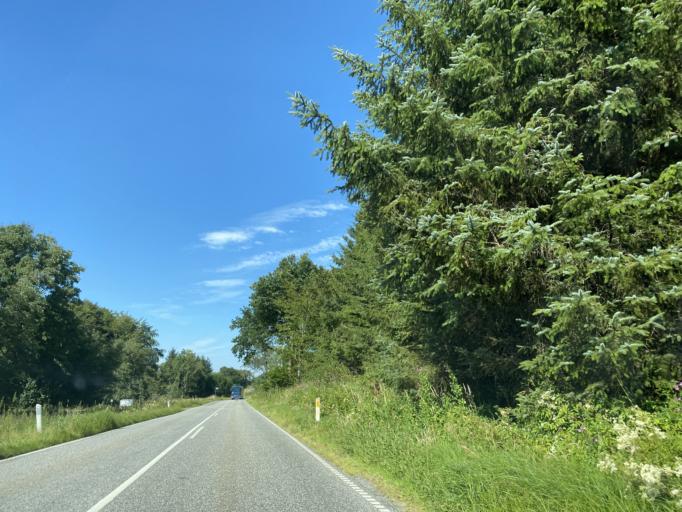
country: DK
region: Central Jutland
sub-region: Hedensted Kommune
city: Torring
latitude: 55.8268
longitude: 9.4389
